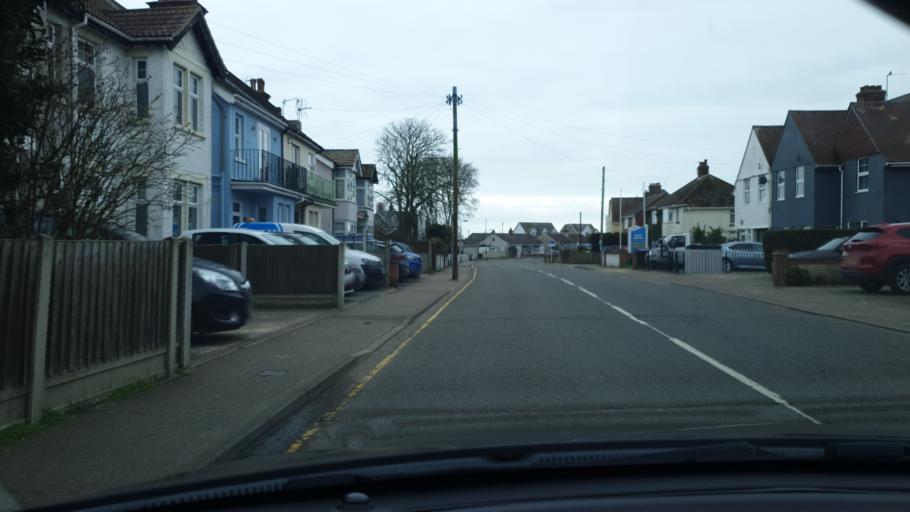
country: GB
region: England
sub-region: Essex
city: Walton-on-the-Naze
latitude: 51.8560
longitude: 1.2788
